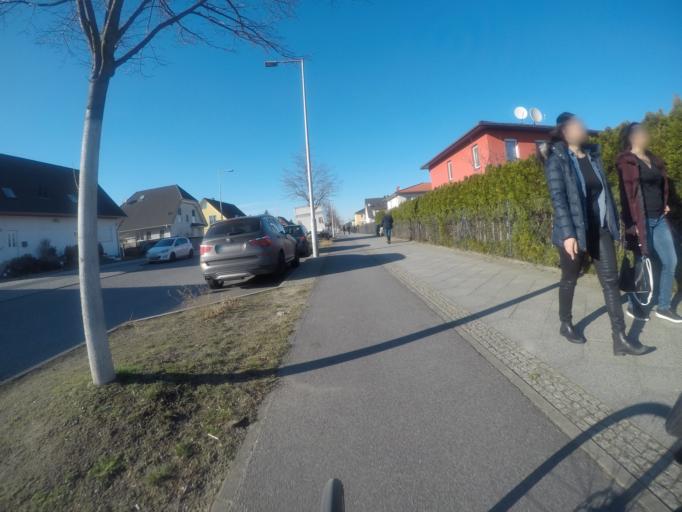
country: DE
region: Berlin
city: Johannisthal
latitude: 52.4306
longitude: 13.5128
